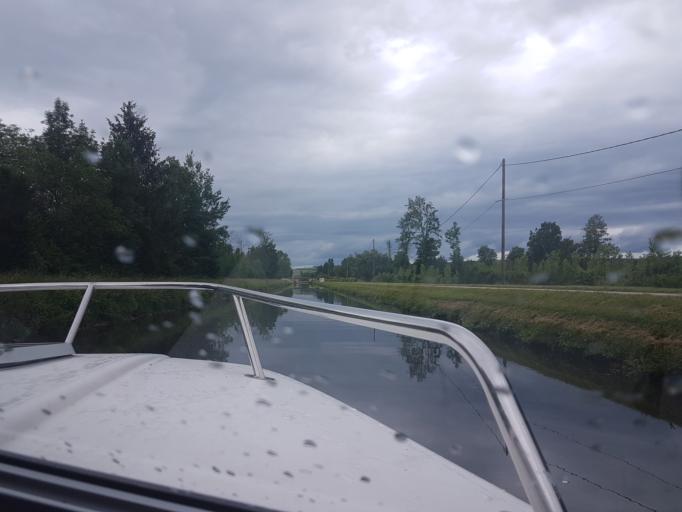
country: FR
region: Bourgogne
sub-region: Departement de l'Yonne
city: Saint-Bris-le-Vineux
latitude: 47.7099
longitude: 3.6364
